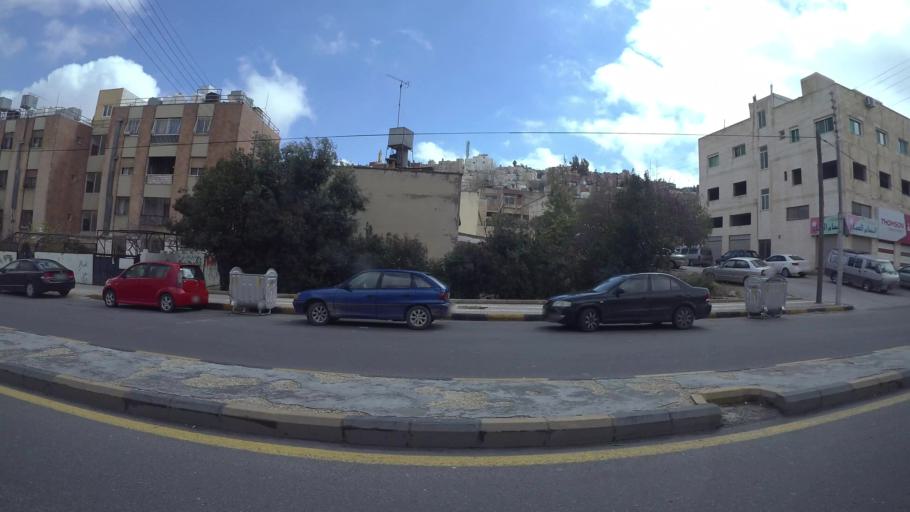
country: JO
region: Amman
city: Al Jubayhah
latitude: 32.0582
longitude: 35.8750
